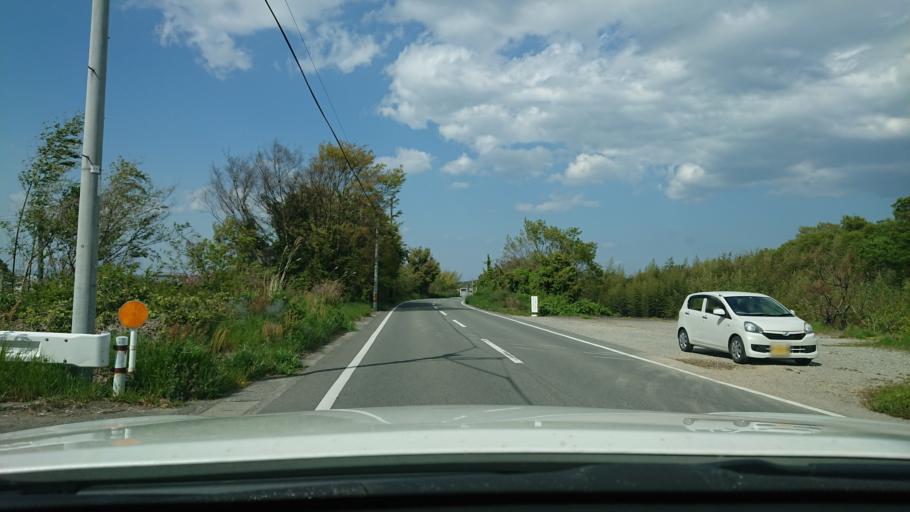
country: JP
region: Tokushima
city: Komatsushimacho
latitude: 34.0064
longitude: 134.5525
